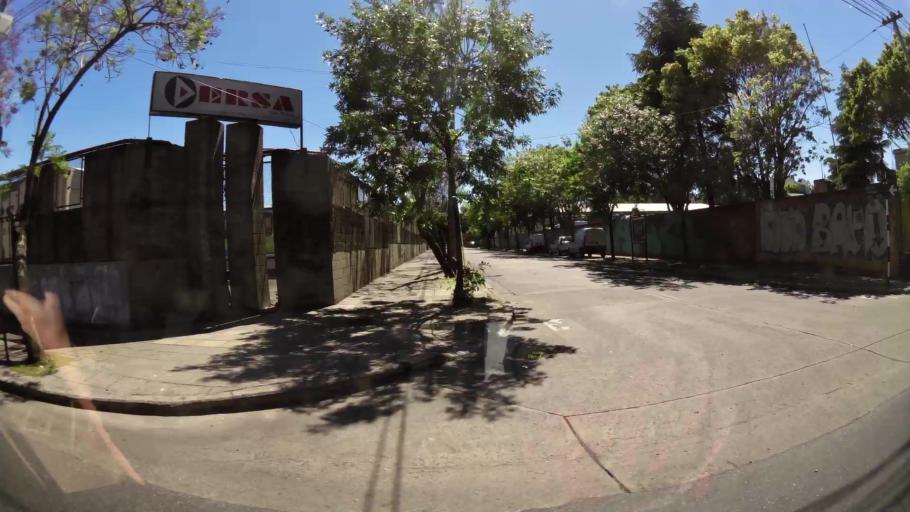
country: AR
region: Buenos Aires
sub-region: Partido de General San Martin
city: General San Martin
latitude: -34.5324
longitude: -58.5447
